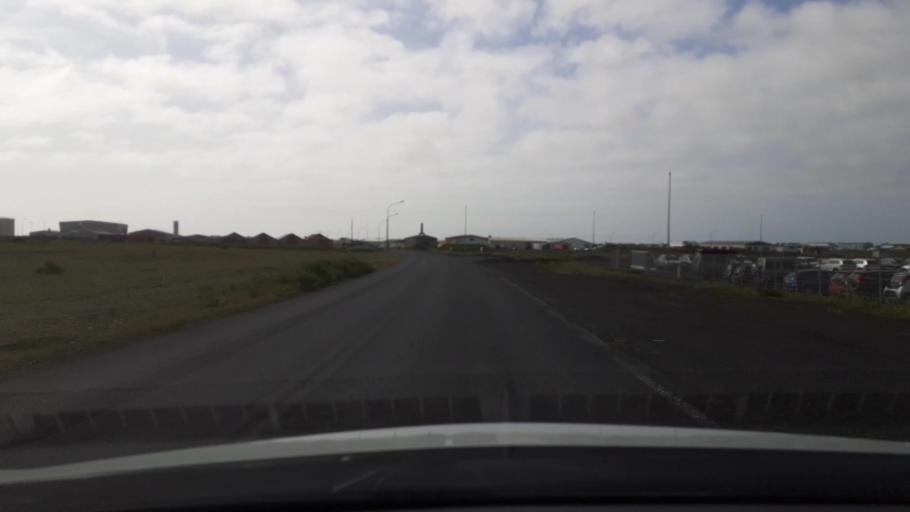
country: IS
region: South
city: THorlakshoefn
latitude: 63.8651
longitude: -21.3828
